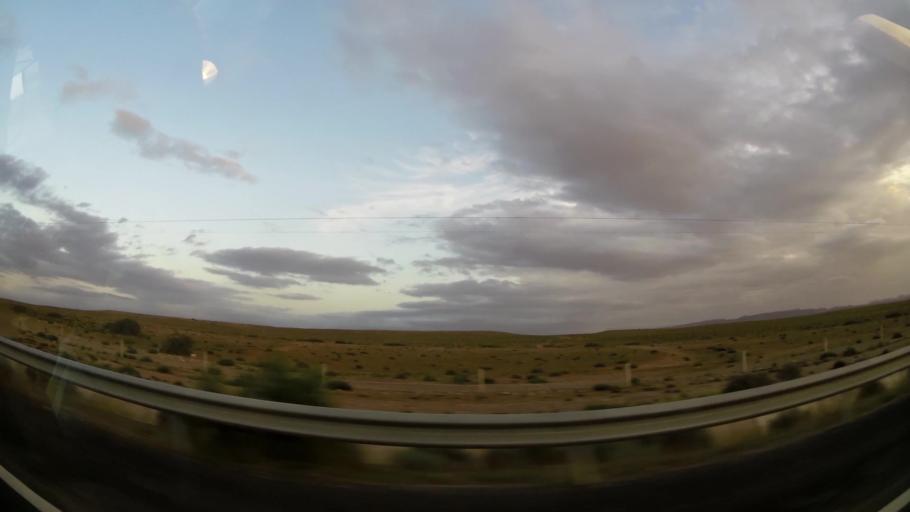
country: MA
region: Oriental
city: Taourirt
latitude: 34.5491
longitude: -2.8811
